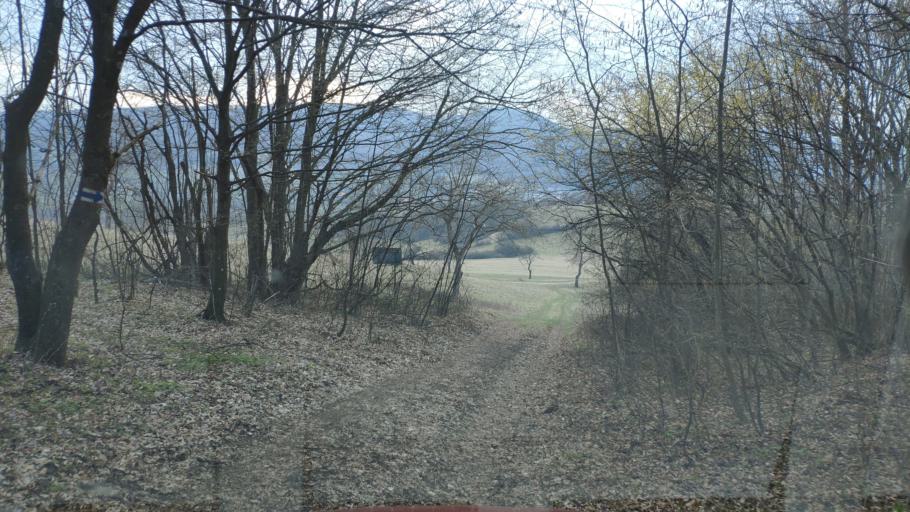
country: SK
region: Kosicky
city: Roznava
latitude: 48.6539
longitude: 20.3932
